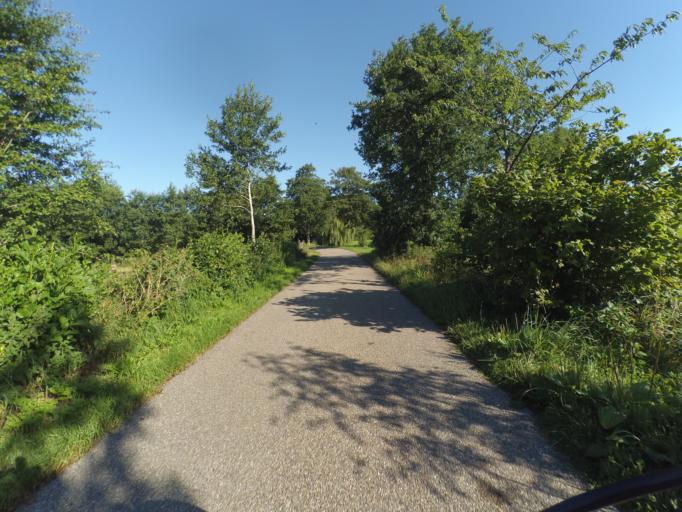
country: NL
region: Friesland
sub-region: Gemeente Achtkarspelen
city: Buitenpost
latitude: 53.2650
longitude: 6.1434
